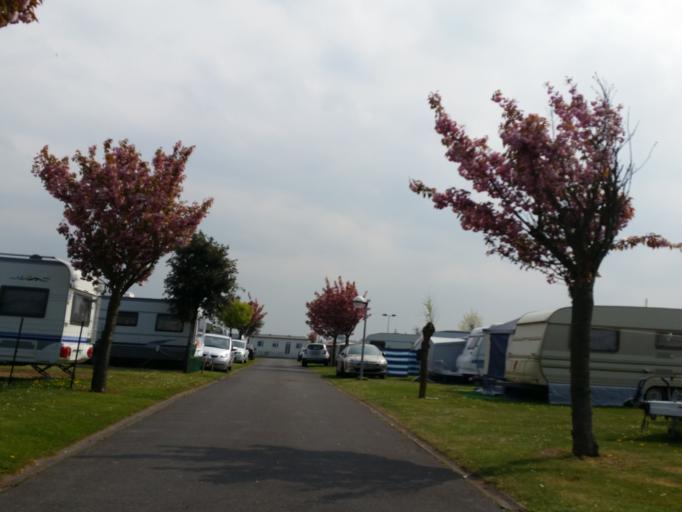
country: BE
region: Flanders
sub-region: Provincie West-Vlaanderen
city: Bredene
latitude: 51.2466
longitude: 2.9683
